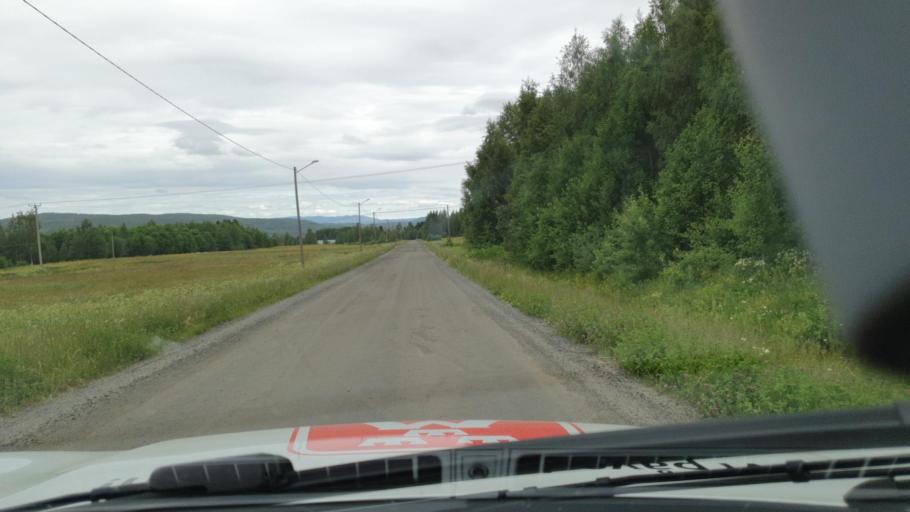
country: SE
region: Vaesterbotten
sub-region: Bjurholms Kommun
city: Bjurholm
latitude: 63.7849
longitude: 19.3767
